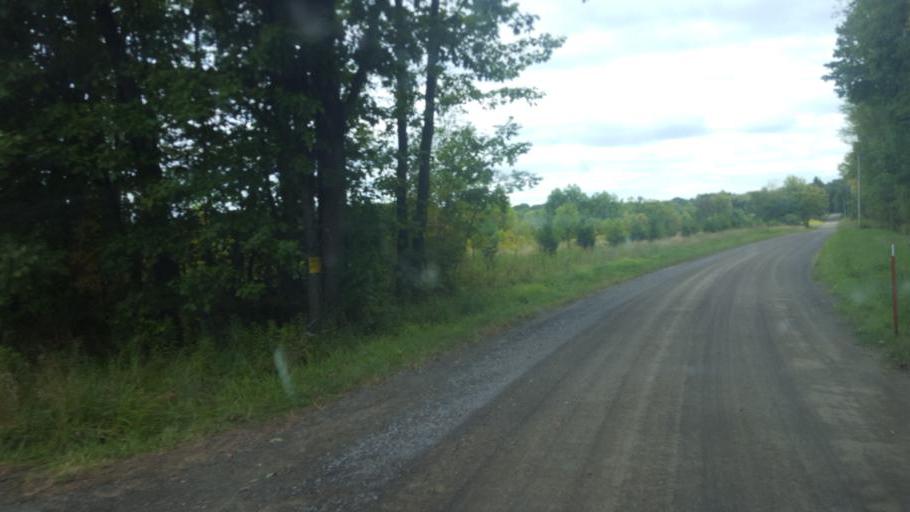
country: US
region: Pennsylvania
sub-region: Crawford County
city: Pymatuning Central
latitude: 41.5425
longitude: -80.4459
